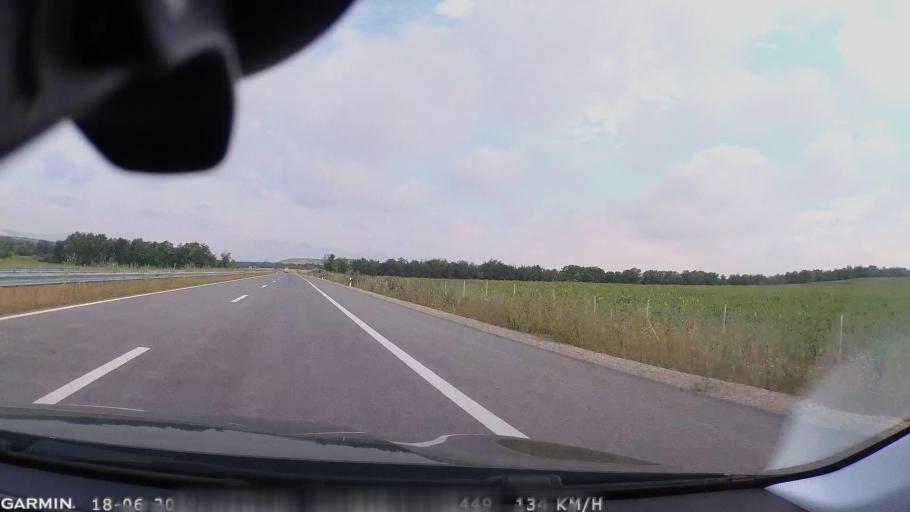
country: MK
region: Sveti Nikole
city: Sveti Nikole
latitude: 41.8386
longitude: 21.9842
